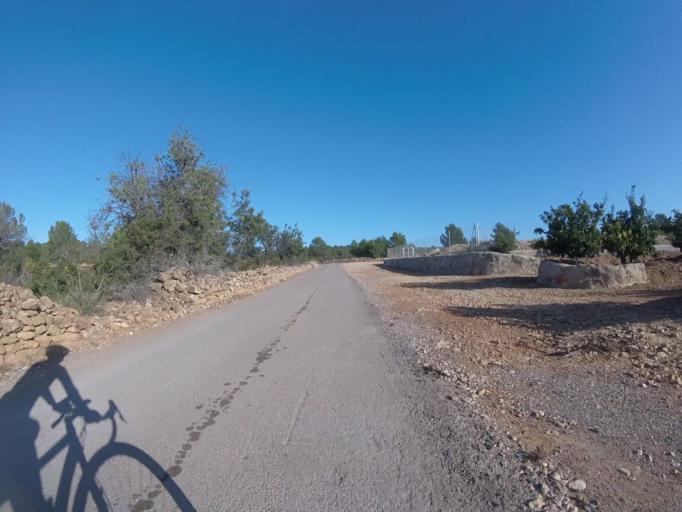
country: ES
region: Valencia
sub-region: Provincia de Castello
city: Alcala de Xivert
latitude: 40.2674
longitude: 0.2080
